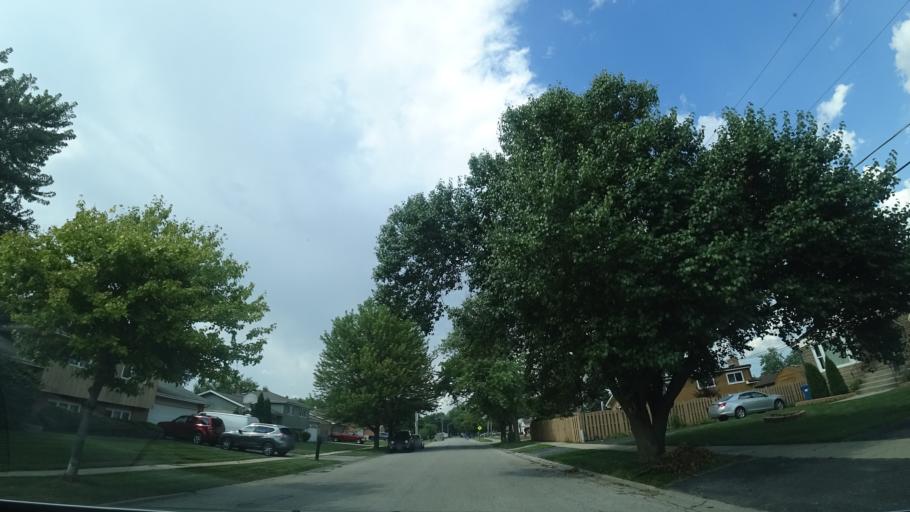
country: US
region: Illinois
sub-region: Cook County
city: Merrionette Park
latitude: 41.6736
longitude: -87.7148
